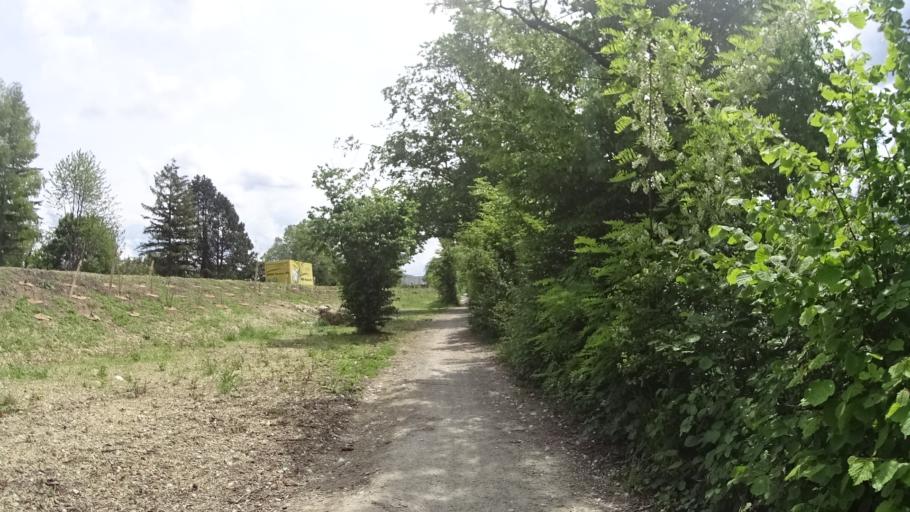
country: CH
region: Basel-Landschaft
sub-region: Bezirk Arlesheim
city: Birsfelden
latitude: 47.5564
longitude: 7.6439
